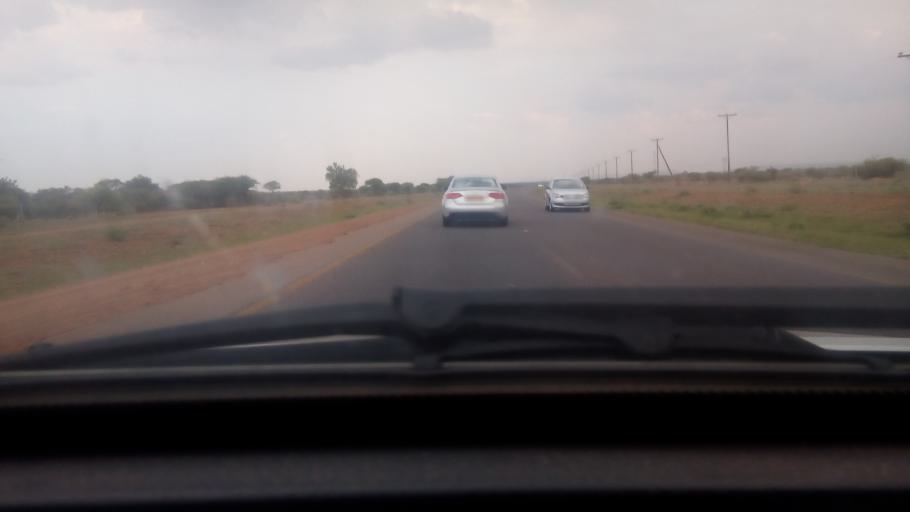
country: BW
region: Kweneng
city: Molepolole
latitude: -24.4554
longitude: 25.6514
